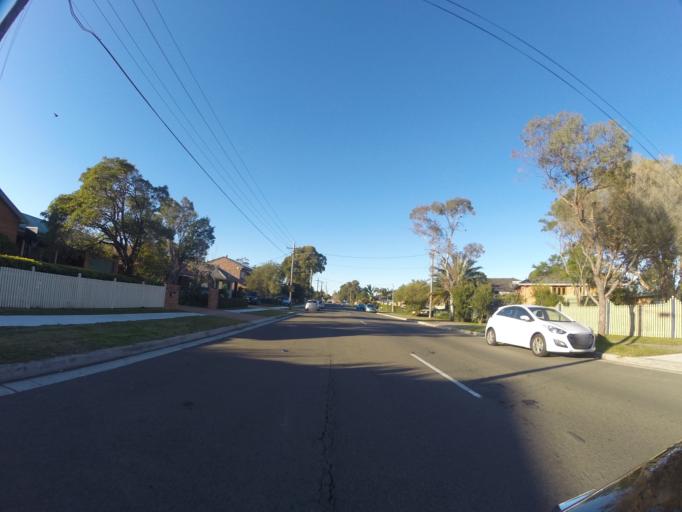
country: AU
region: New South Wales
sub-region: Sutherland Shire
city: Gymea Bay
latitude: -34.0499
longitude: 151.0875
